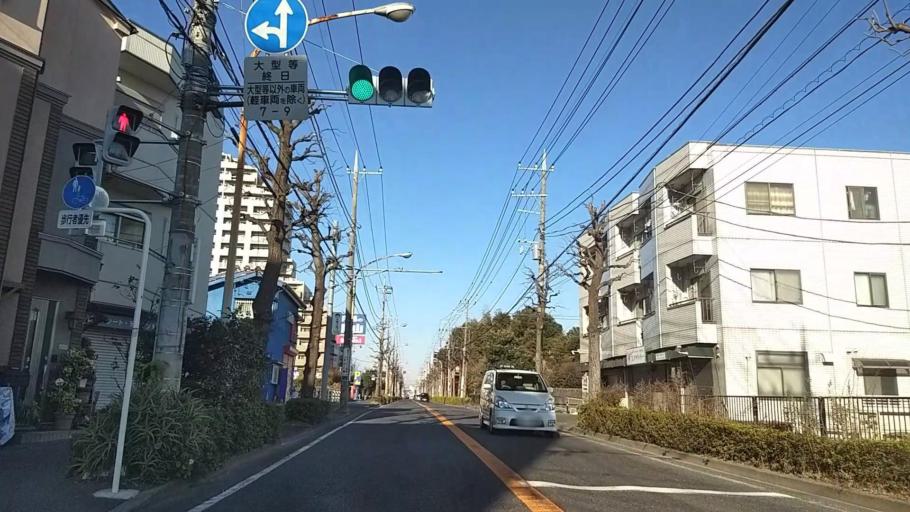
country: JP
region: Tokyo
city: Chofugaoka
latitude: 35.6082
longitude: 139.6069
